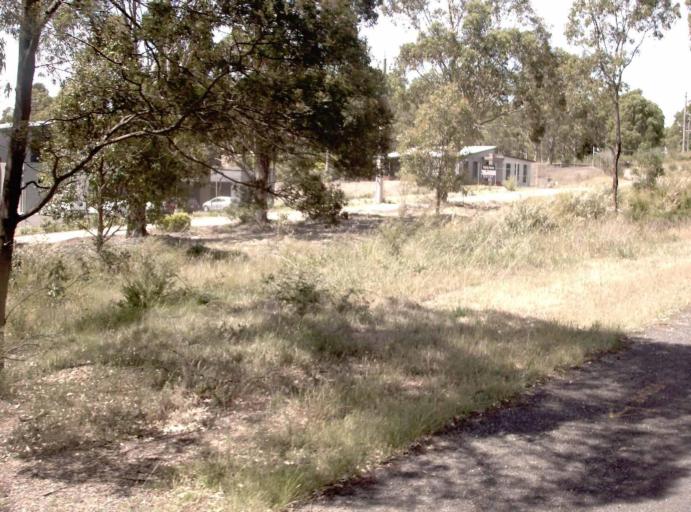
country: AU
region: Victoria
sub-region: Wellington
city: Sale
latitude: -37.9615
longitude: 147.0921
